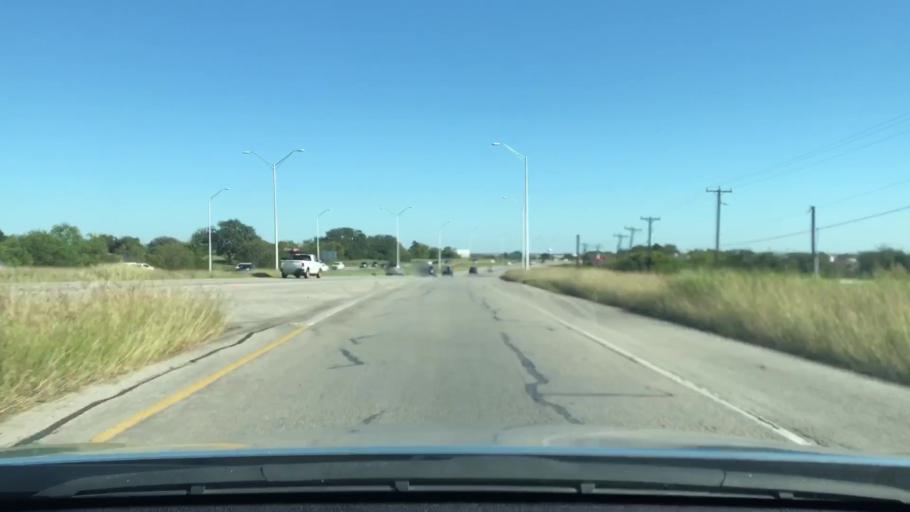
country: US
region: Texas
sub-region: Bexar County
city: Universal City
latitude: 29.5442
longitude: -98.3120
